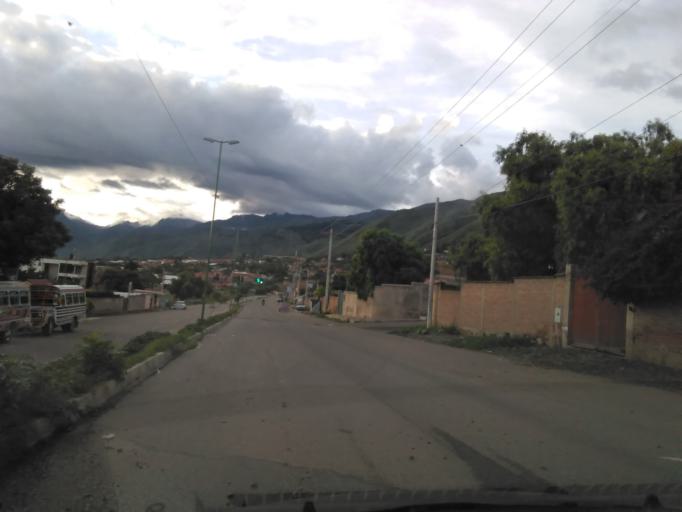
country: BO
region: Cochabamba
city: Cochabamba
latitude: -17.3457
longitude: -66.1743
